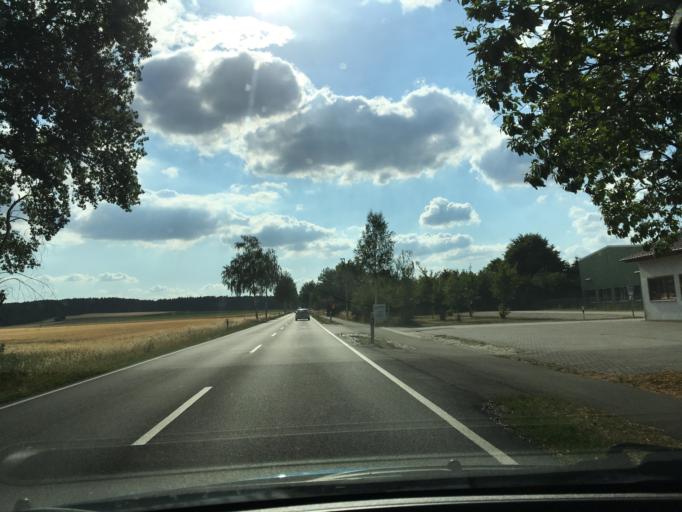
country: DE
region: Lower Saxony
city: Karwitz
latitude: 53.0836
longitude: 11.0130
